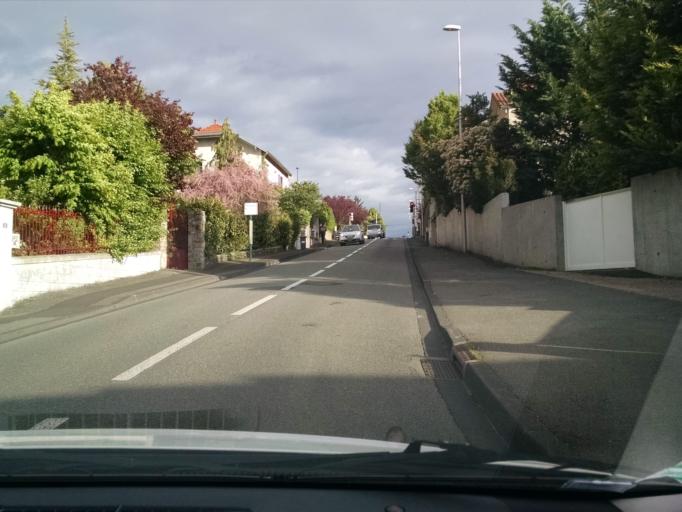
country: FR
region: Auvergne
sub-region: Departement du Puy-de-Dome
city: Royat
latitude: 45.7608
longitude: 3.0618
